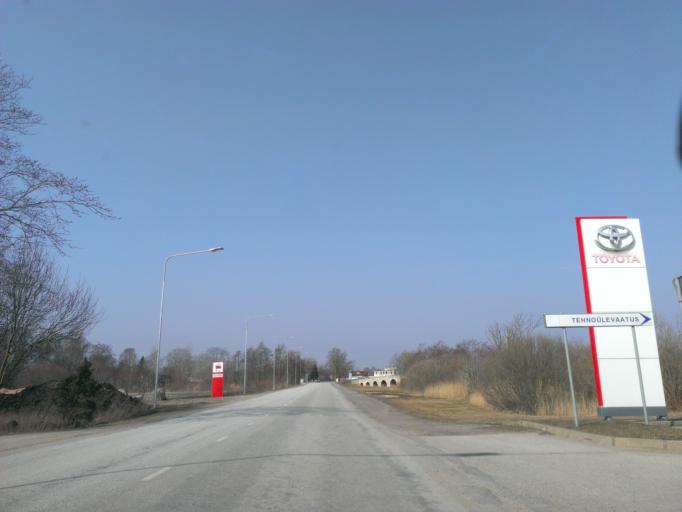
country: EE
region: Saare
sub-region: Kuressaare linn
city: Kuressaare
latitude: 58.2633
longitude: 22.4800
